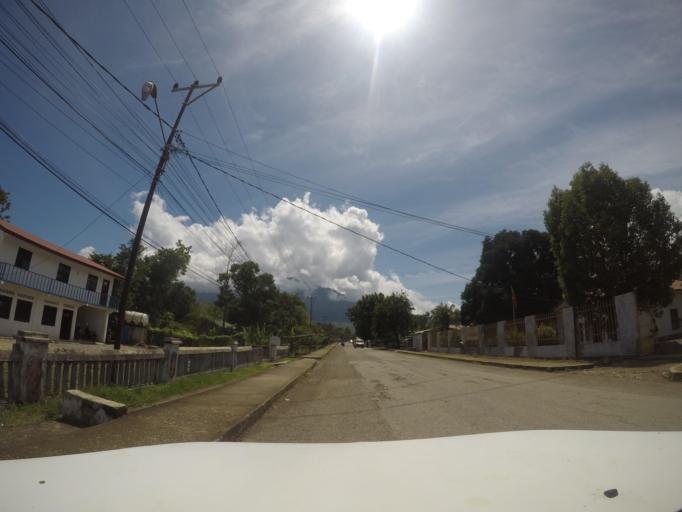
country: TL
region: Bobonaro
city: Maliana
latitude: -8.9890
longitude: 125.2123
